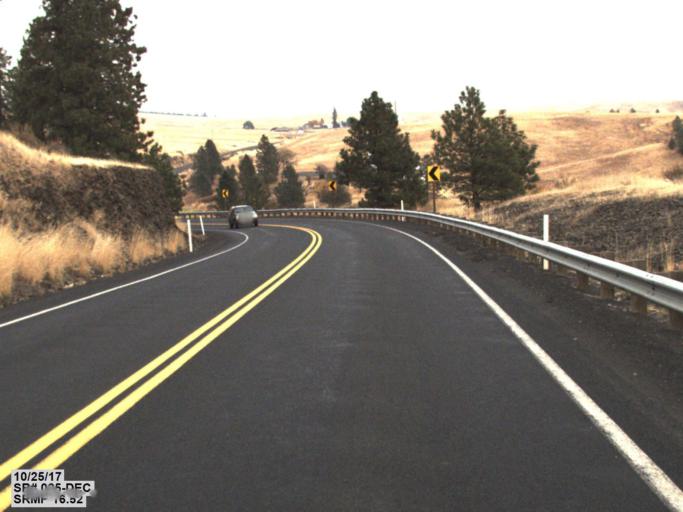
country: US
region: Washington
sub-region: Lincoln County
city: Davenport
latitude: 47.8609
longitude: -118.2351
